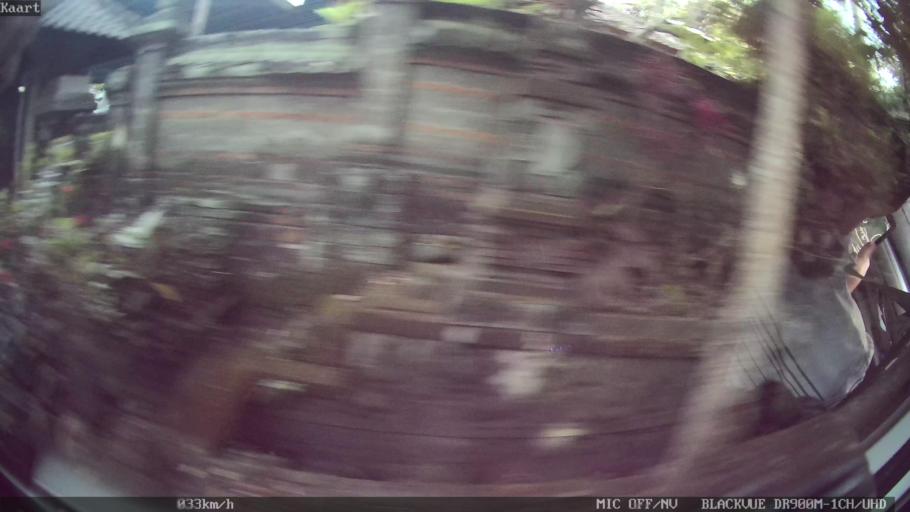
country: ID
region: Bali
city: Banjar Karangsuling
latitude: -8.6097
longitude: 115.2029
